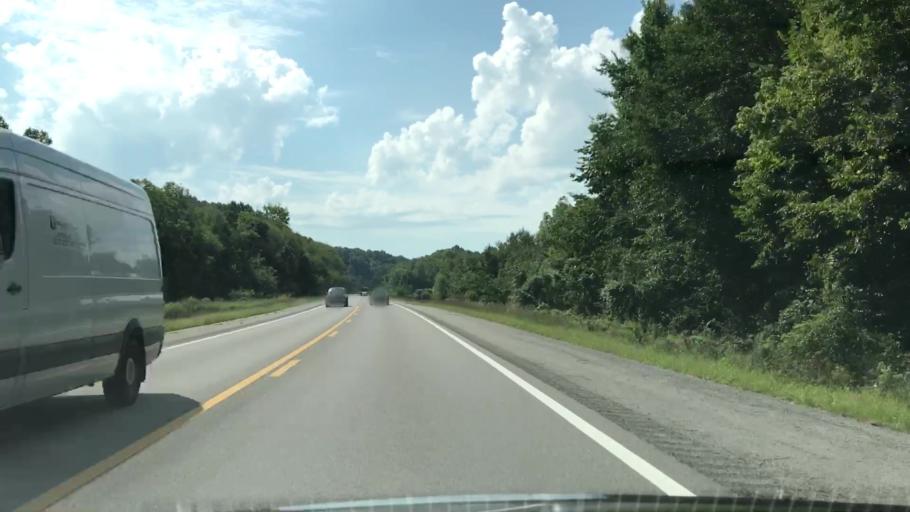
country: US
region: Tennessee
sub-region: Sumner County
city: Westmoreland
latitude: 36.6335
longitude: -86.2416
